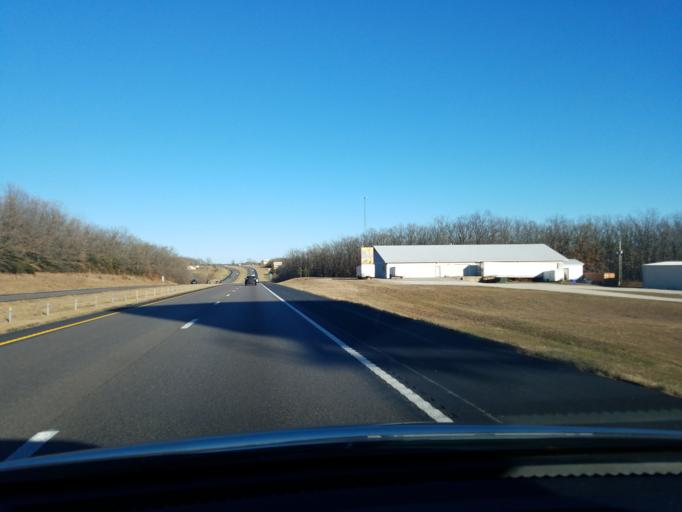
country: US
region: Missouri
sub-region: Phelps County
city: Saint James
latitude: 38.0129
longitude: -91.5932
